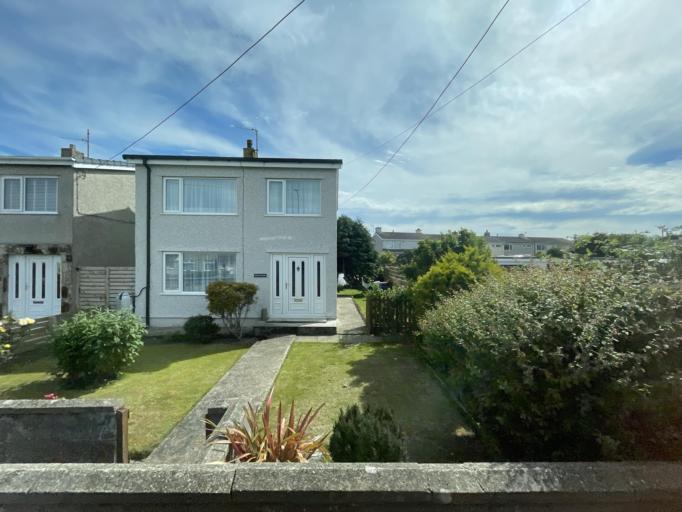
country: GB
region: Wales
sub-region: Anglesey
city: Valley
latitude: 53.2768
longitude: -4.5420
